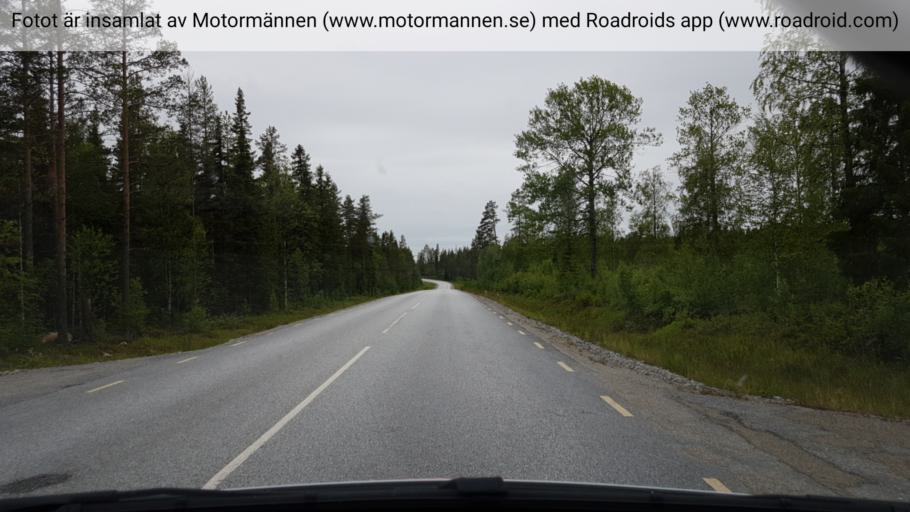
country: SE
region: Vaesterbotten
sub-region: Bjurholms Kommun
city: Bjurholm
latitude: 64.1717
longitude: 19.3955
